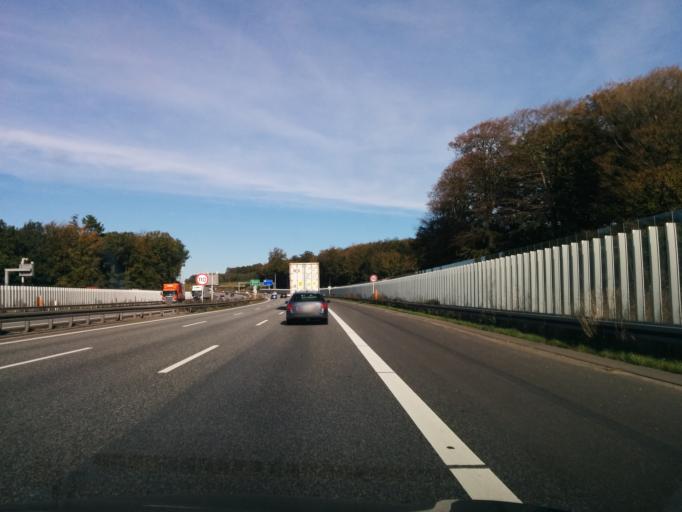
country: DK
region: South Denmark
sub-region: Vejle Kommune
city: Vejle
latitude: 55.7075
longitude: 9.5763
